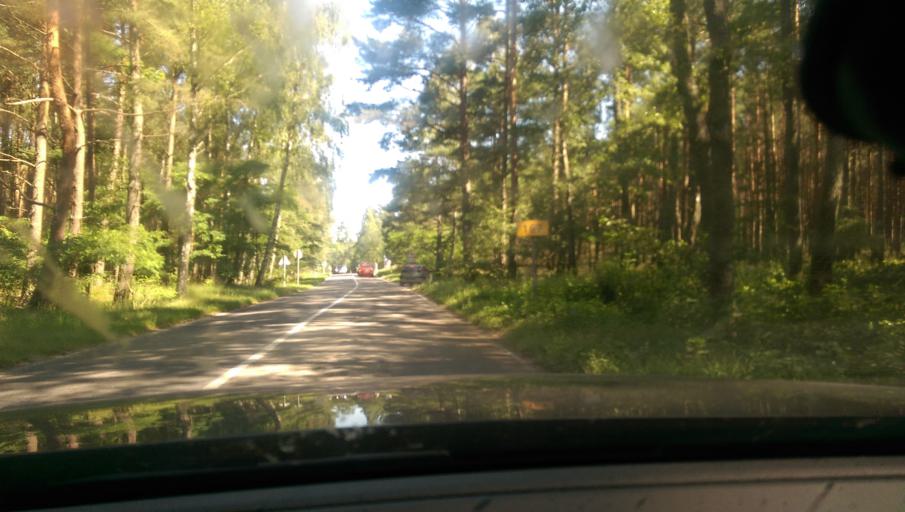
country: LT
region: Klaipedos apskritis
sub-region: Klaipeda
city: Klaipeda
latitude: 55.6795
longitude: 21.1133
